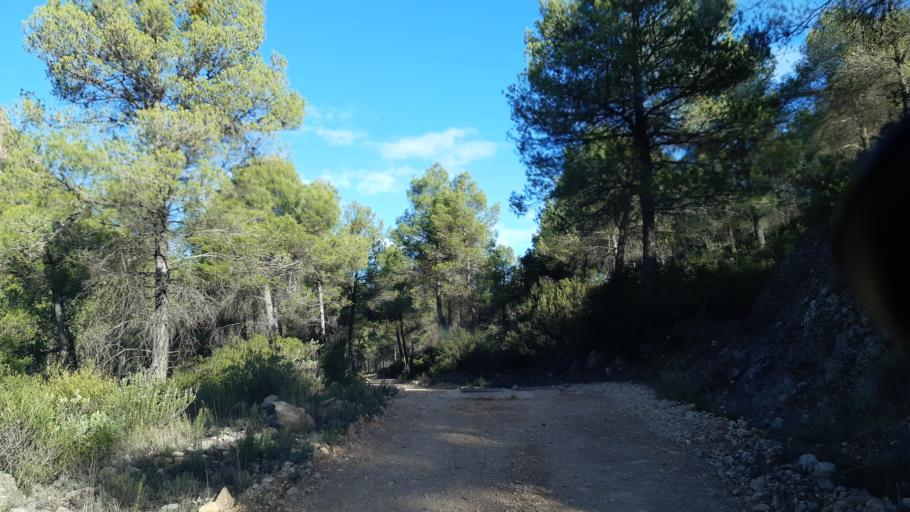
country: ES
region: Aragon
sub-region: Provincia de Teruel
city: Lledo
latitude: 40.8682
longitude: 0.2543
